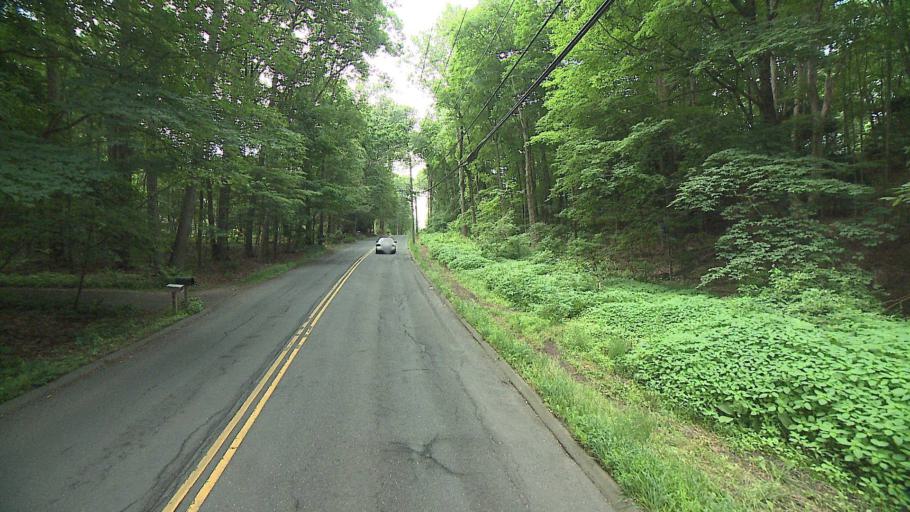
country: US
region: Connecticut
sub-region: New Haven County
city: Southbury
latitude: 41.4647
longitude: -73.2017
